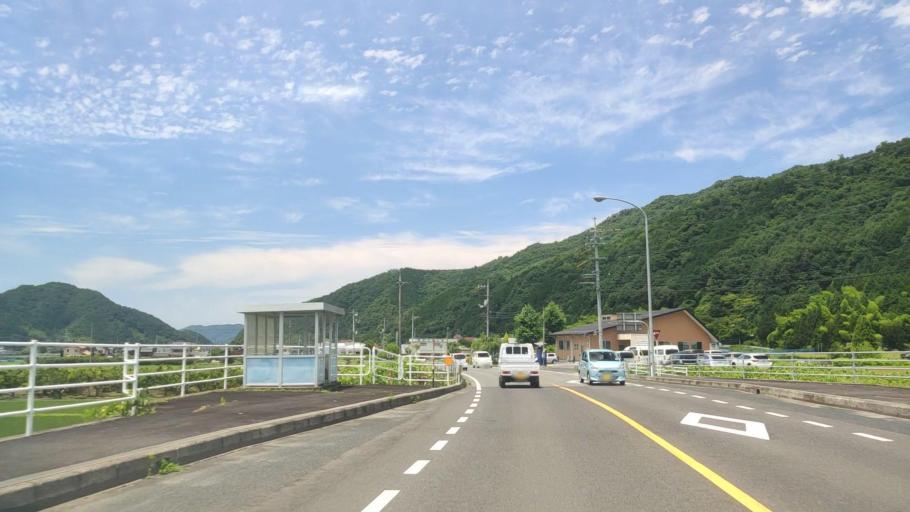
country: JP
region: Tottori
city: Tottori
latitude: 35.3721
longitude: 134.3082
